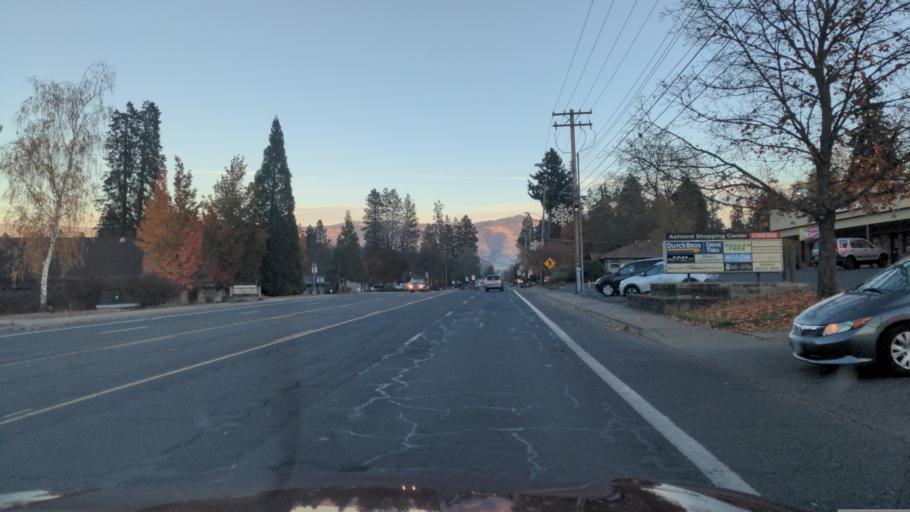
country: US
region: Oregon
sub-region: Jackson County
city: Ashland
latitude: 42.1854
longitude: -122.6862
